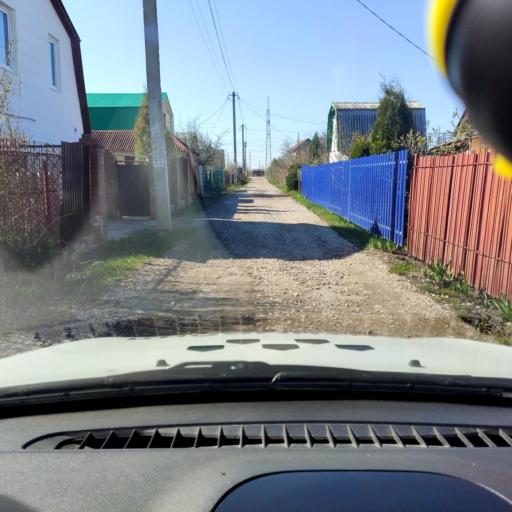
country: RU
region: Samara
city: Tol'yatti
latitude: 53.5929
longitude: 49.2934
